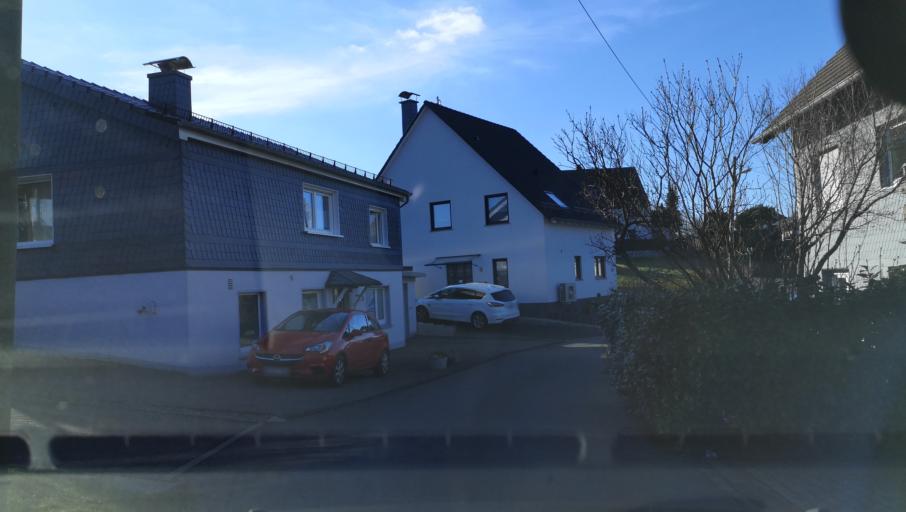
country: DE
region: North Rhine-Westphalia
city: Radevormwald
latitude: 51.2233
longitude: 7.3581
